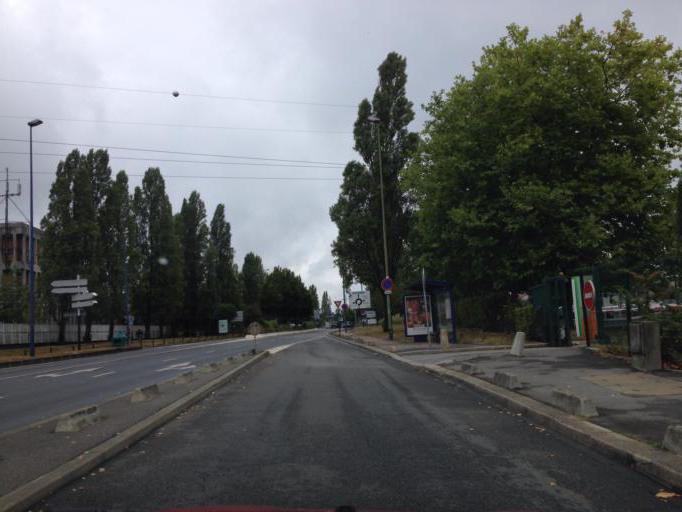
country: FR
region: Ile-de-France
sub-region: Departement des Hauts-de-Seine
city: Le Plessis-Robinson
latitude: 48.7882
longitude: 2.2531
